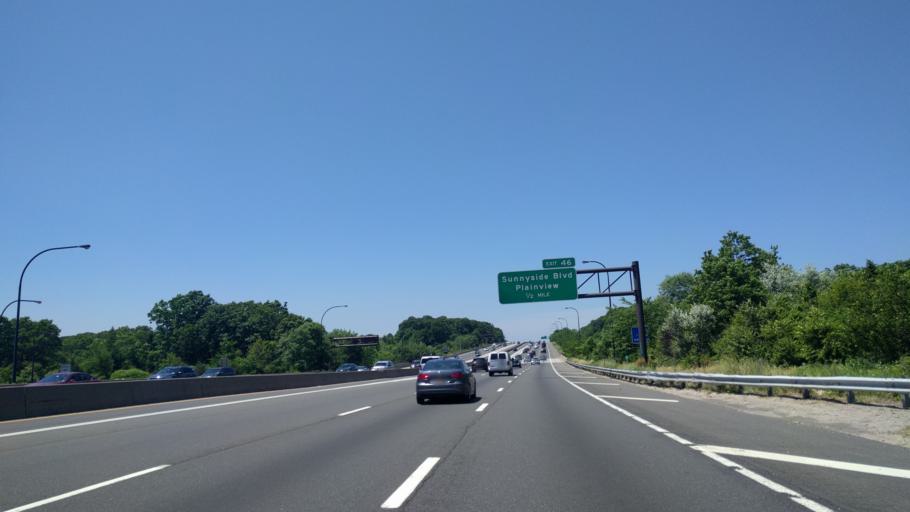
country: US
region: New York
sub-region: Nassau County
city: Plainview
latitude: 40.7885
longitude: -73.4537
